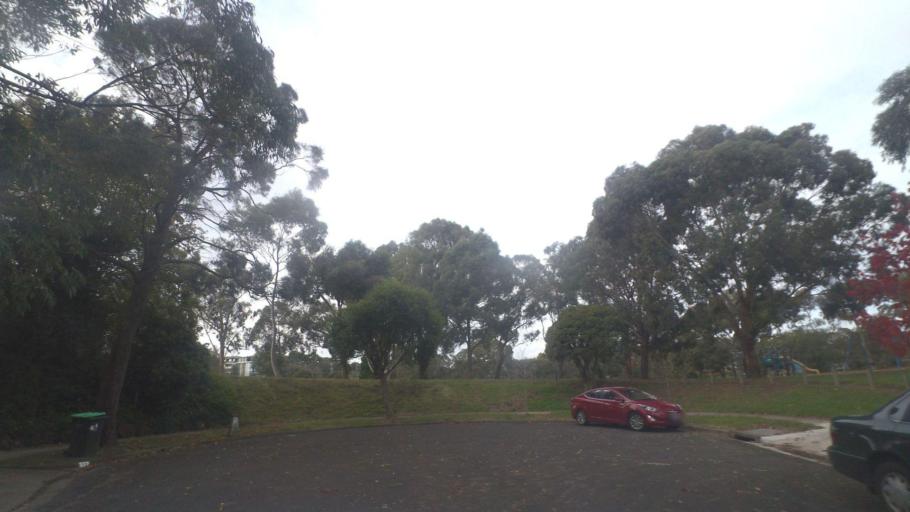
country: AU
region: Victoria
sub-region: Whitehorse
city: Vermont South
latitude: -37.8564
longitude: 145.1731
